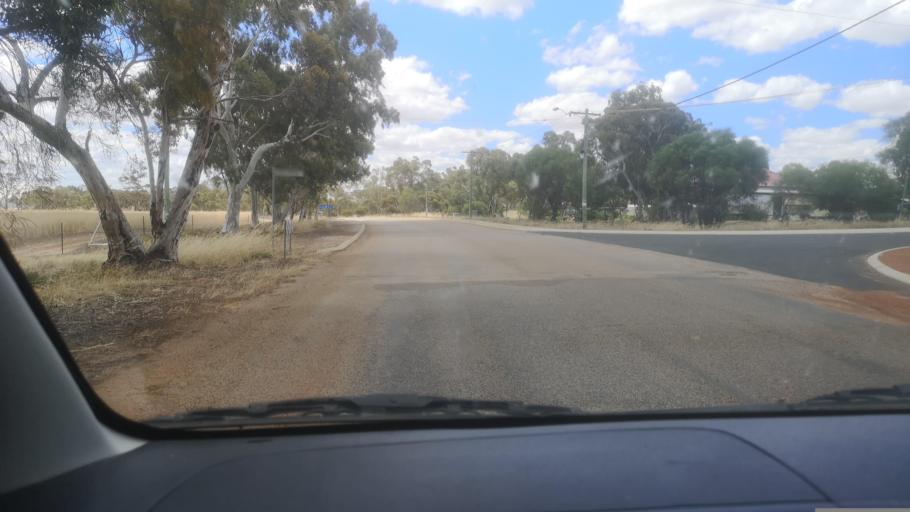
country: AU
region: Western Australia
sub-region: Cunderdin
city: Cunderdin
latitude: -32.0180
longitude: 117.3977
